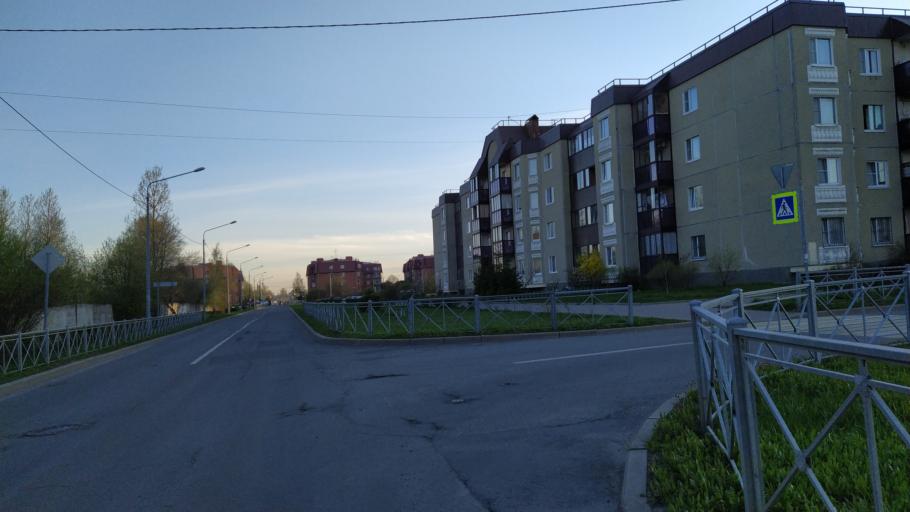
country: RU
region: St.-Petersburg
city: Pushkin
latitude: 59.7030
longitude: 30.3844
